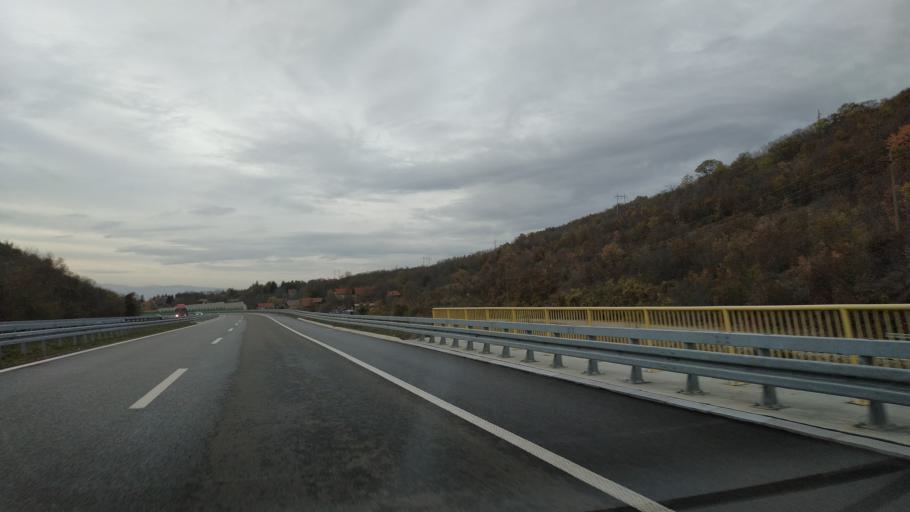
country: RS
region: Central Serbia
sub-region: Nisavski Okrug
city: Niska Banja
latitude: 43.2999
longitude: 22.0629
